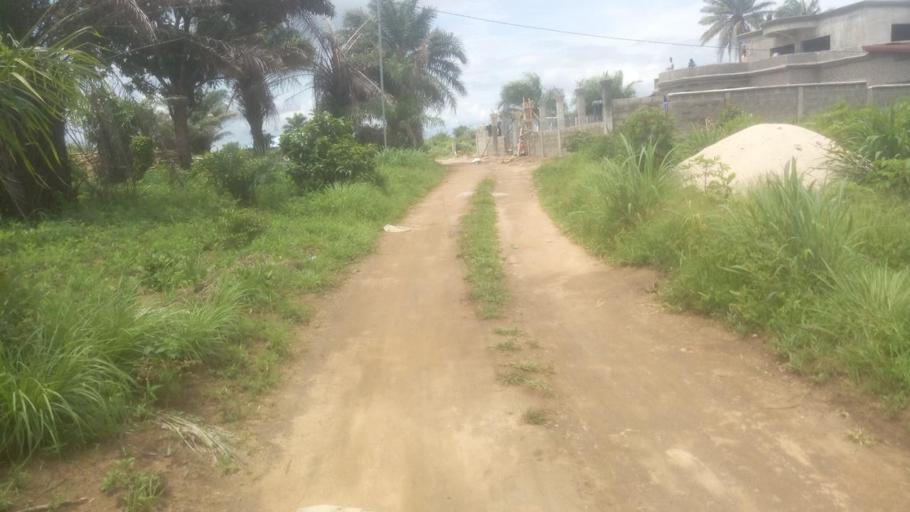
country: SL
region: Northern Province
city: Masoyila
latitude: 8.5518
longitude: -13.1584
